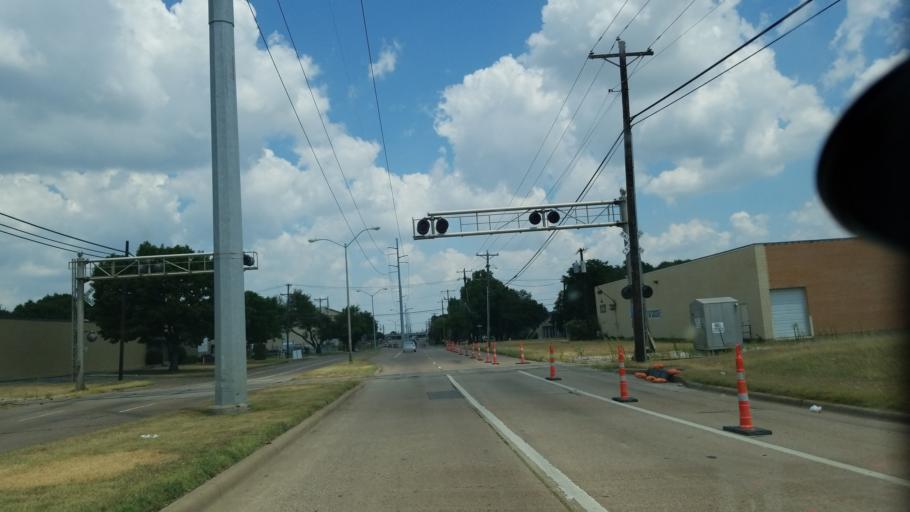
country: US
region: Texas
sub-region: Dallas County
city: Duncanville
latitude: 32.6861
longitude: -96.8914
